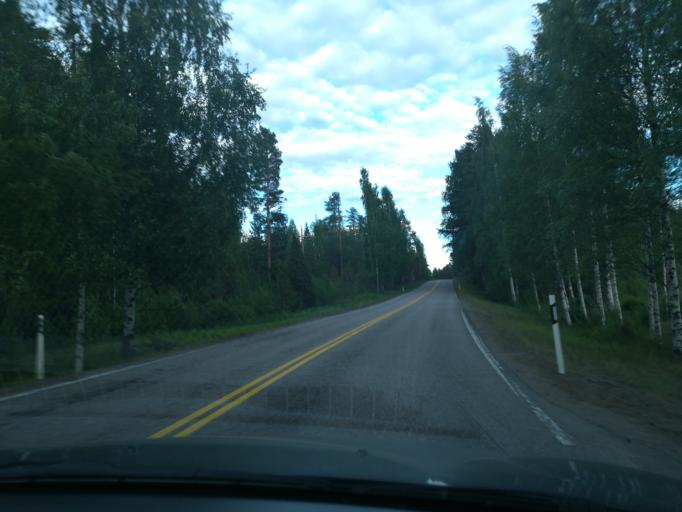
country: FI
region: Southern Savonia
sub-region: Mikkeli
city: Puumala
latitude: 61.5633
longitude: 27.9941
